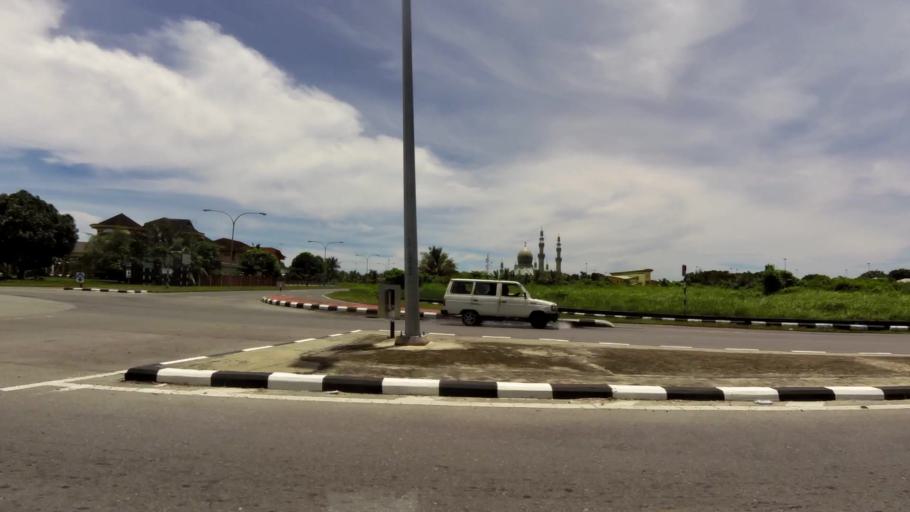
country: BN
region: Belait
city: Kuala Belait
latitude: 4.5819
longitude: 114.2324
